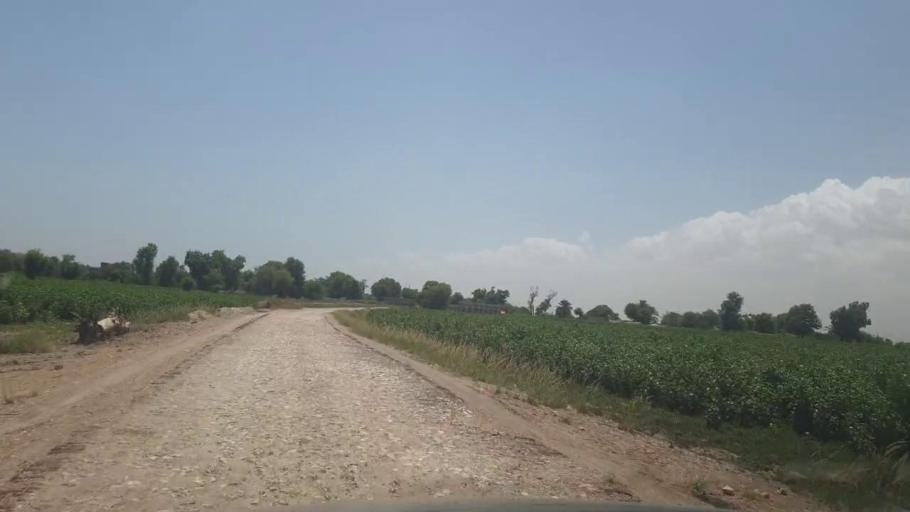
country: PK
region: Sindh
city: Kot Diji
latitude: 27.2672
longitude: 69.0189
